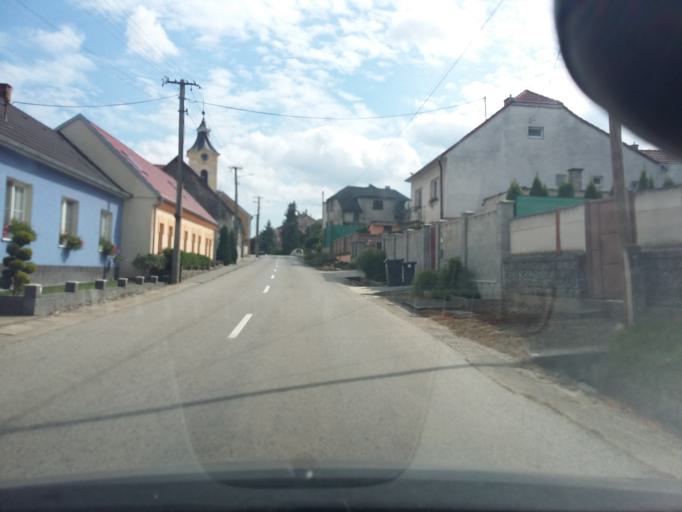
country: SK
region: Trnavsky
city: Gbely
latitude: 48.7224
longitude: 17.1607
